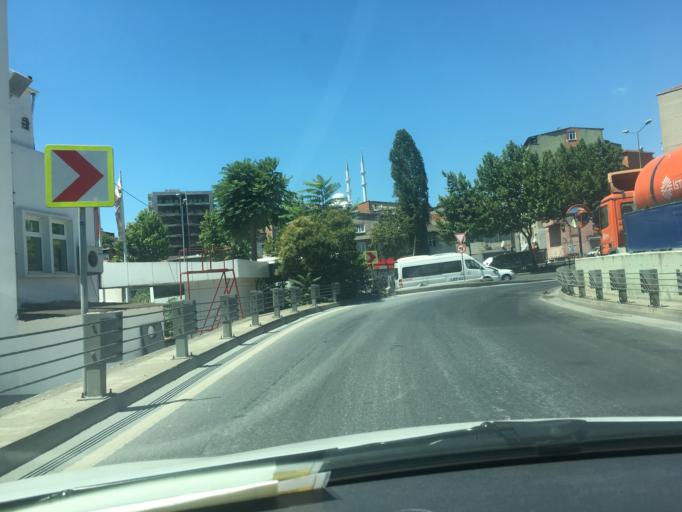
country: TR
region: Istanbul
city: Sisli
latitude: 41.0481
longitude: 28.9687
